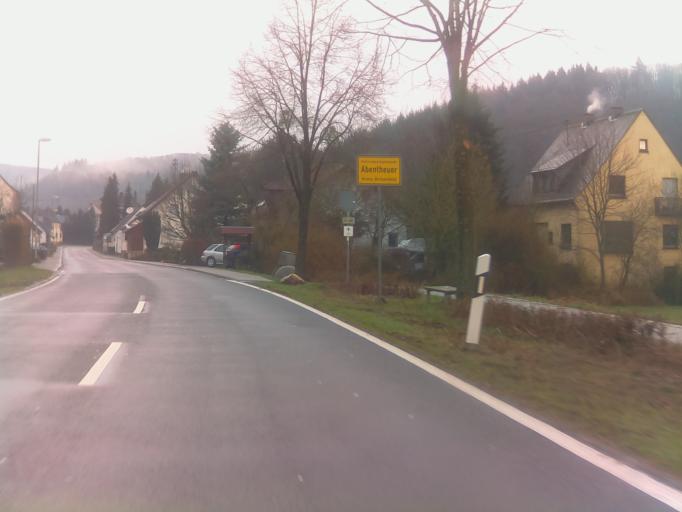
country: DE
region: Rheinland-Pfalz
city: Abentheuer
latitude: 49.6454
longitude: 7.1053
